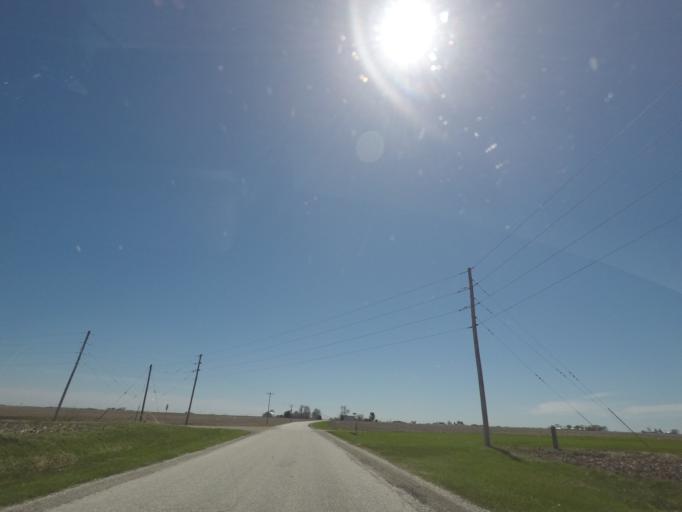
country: US
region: Illinois
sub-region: Logan County
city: Mount Pulaski
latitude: 40.0488
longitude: -89.1823
